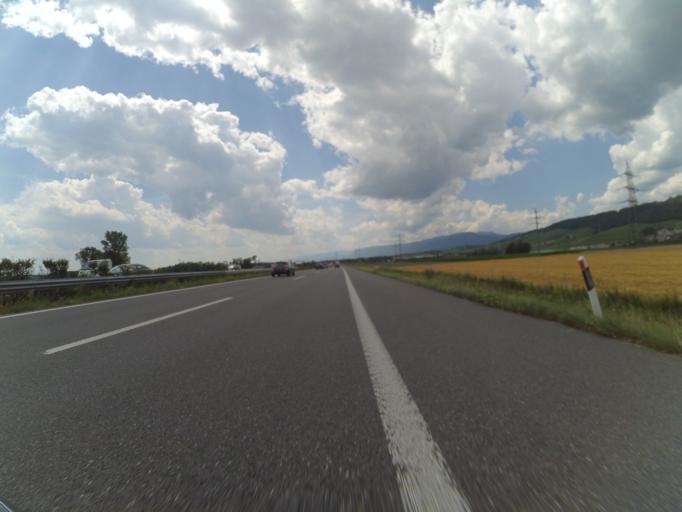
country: CH
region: Vaud
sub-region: Nyon District
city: Gland
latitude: 46.4436
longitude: 6.2917
